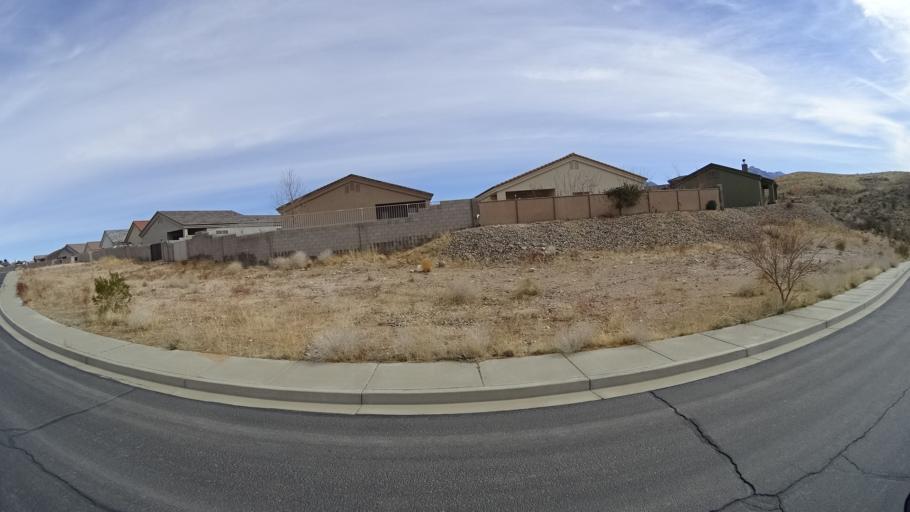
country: US
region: Arizona
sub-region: Mohave County
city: Kingman
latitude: 35.1855
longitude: -114.0189
